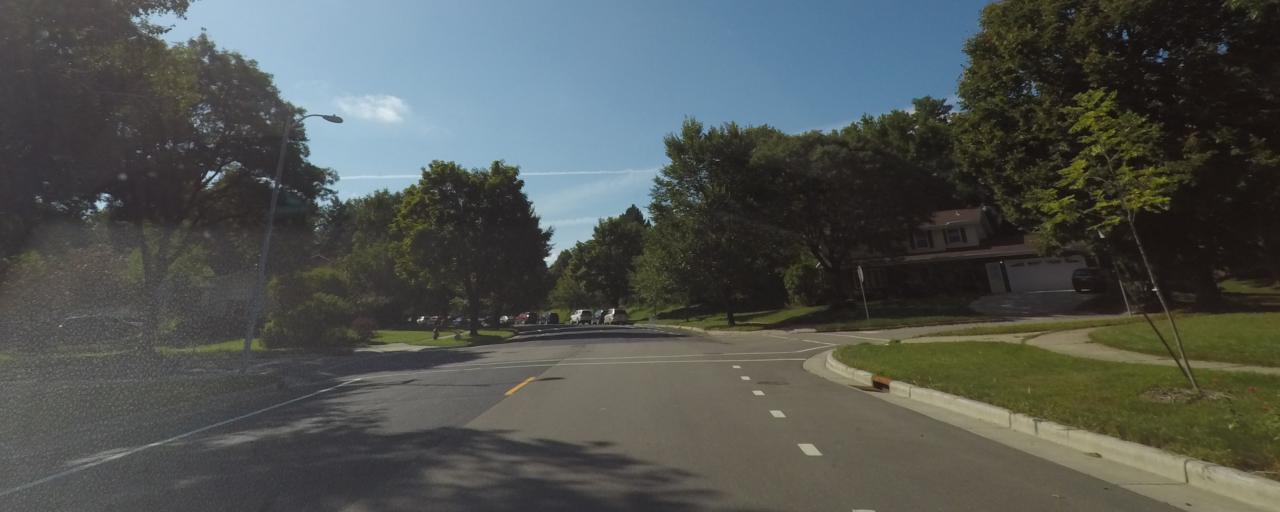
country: US
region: Wisconsin
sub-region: Dane County
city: Middleton
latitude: 43.0712
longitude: -89.5105
